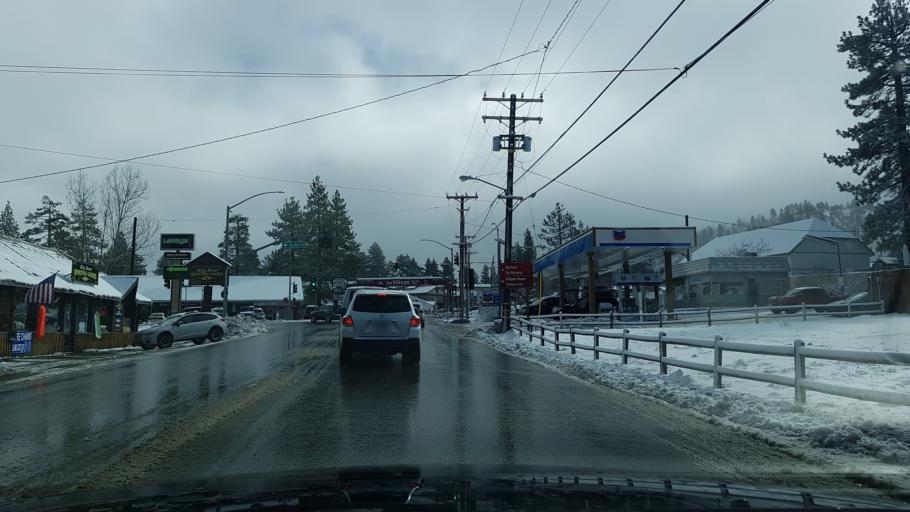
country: US
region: California
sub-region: San Bernardino County
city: Big Bear Lake
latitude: 34.2414
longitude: -116.9179
